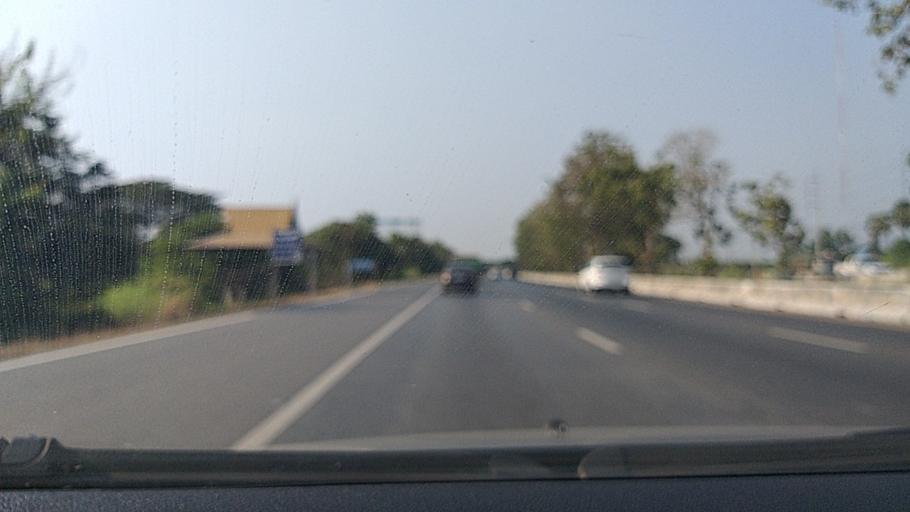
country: TH
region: Ang Thong
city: Chaiyo
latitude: 14.6934
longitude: 100.4586
